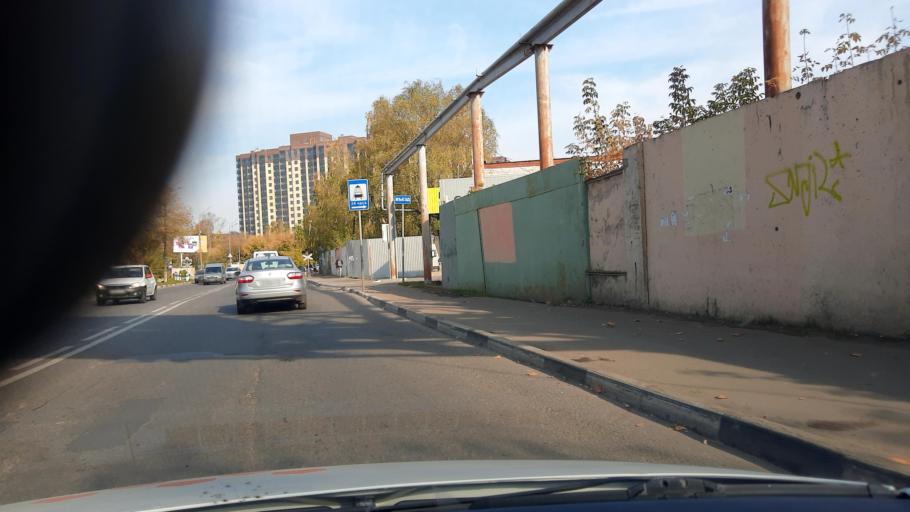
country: RU
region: Moskovskaya
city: Elektrostal'
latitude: 55.8009
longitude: 38.4515
